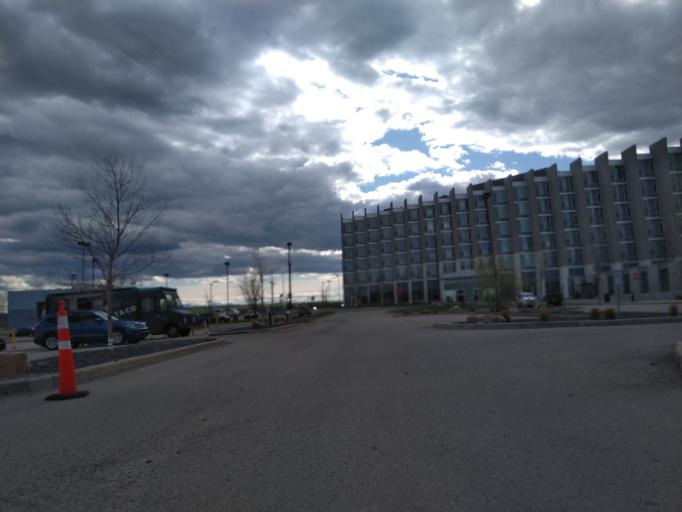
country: CA
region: Alberta
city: Calgary
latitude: 51.0069
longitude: -114.1471
